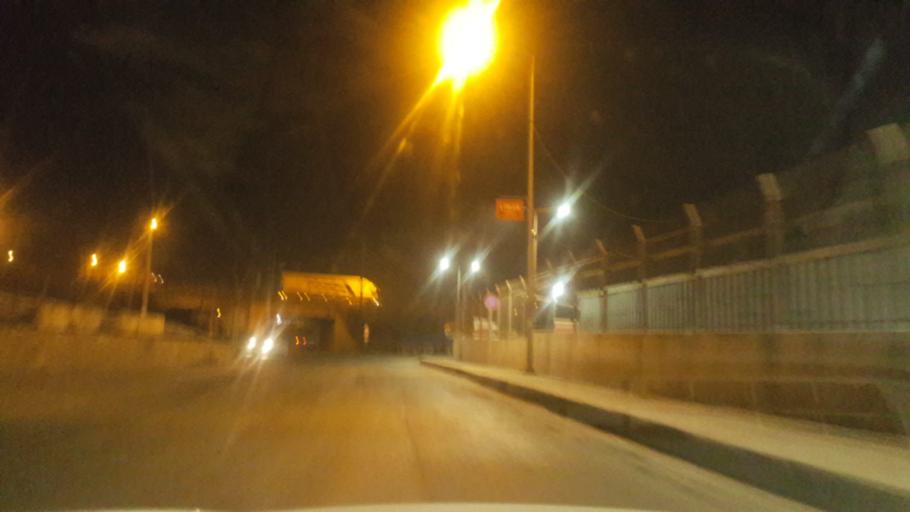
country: TR
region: Kocaeli
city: Tavsancil
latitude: 40.7753
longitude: 29.5299
